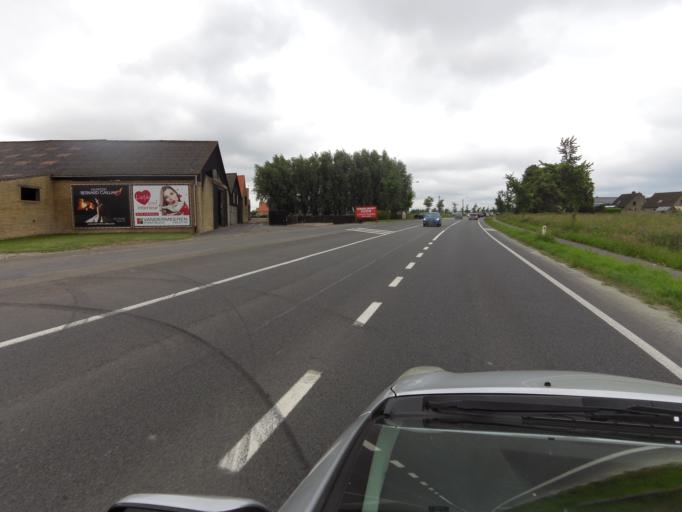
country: BE
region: Flanders
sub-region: Provincie West-Vlaanderen
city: Diksmuide
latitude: 51.0786
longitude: 2.8750
